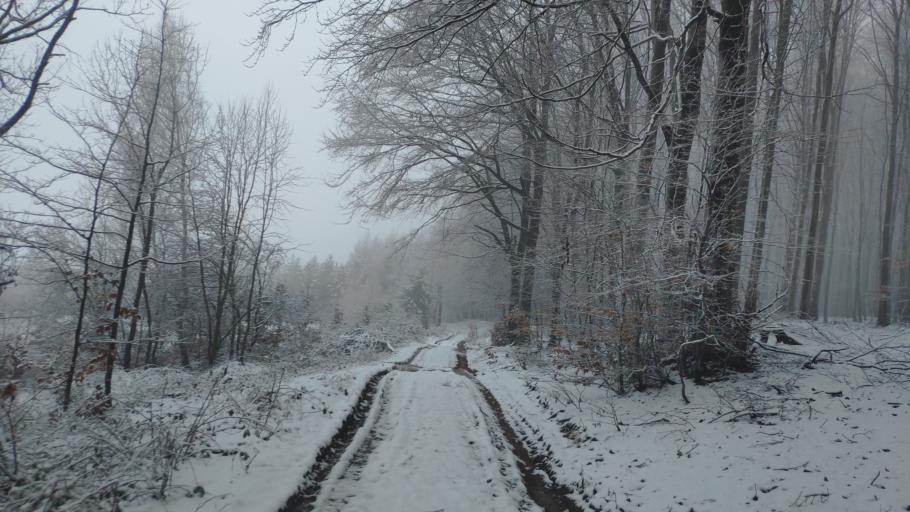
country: SK
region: Kosicky
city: Moldava nad Bodvou
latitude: 48.7440
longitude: 21.0800
